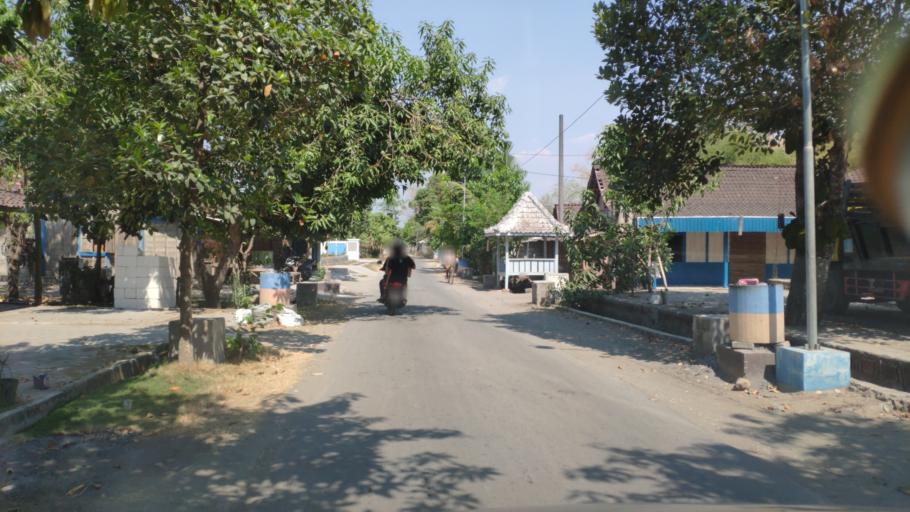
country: ID
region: Central Java
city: Ketuwan
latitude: -7.2348
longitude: 111.5104
